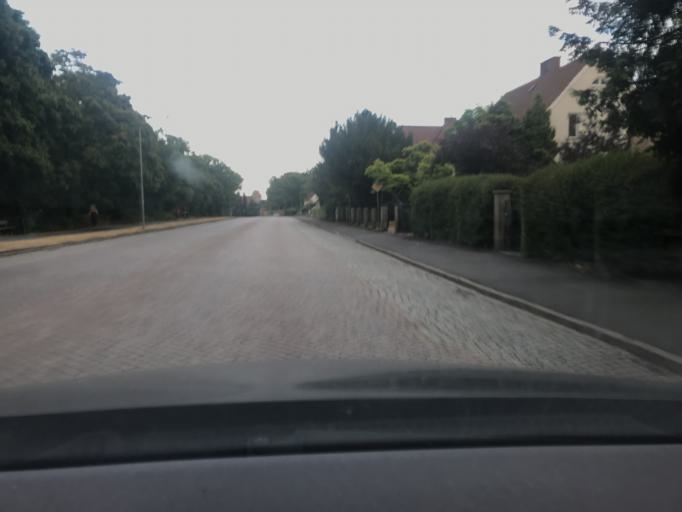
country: SE
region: Skane
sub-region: Simrishamns Kommun
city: Simrishamn
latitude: 55.5615
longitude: 14.3394
